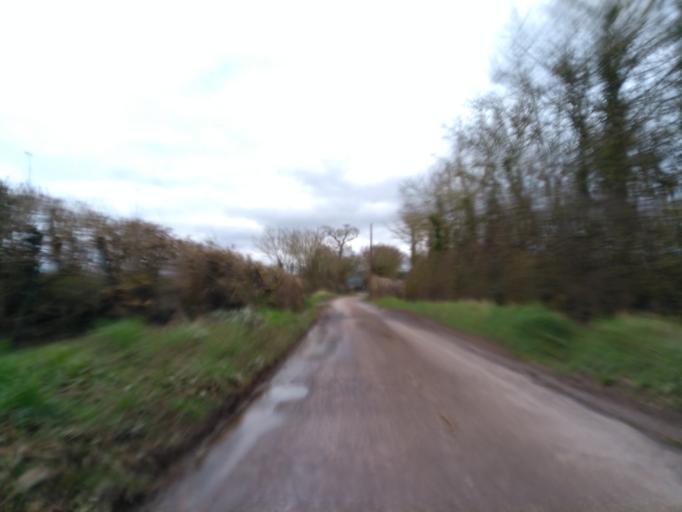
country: GB
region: England
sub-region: Devon
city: Heavitree
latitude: 50.7884
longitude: -3.5022
